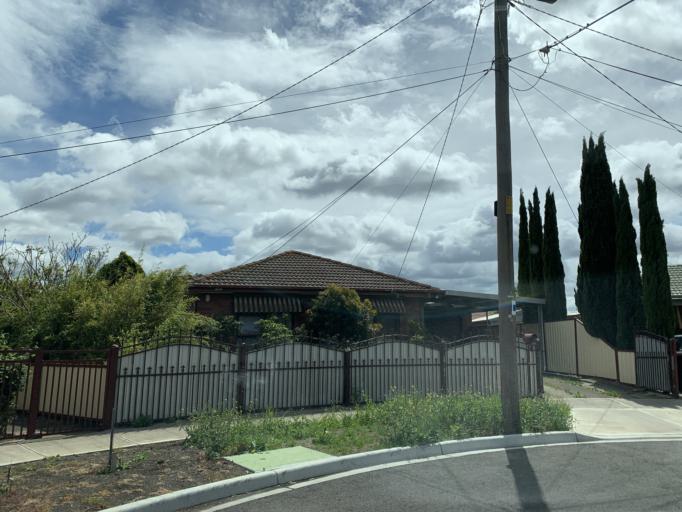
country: AU
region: Victoria
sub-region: Brimbank
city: Cairnlea
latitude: -37.7615
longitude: 144.8029
